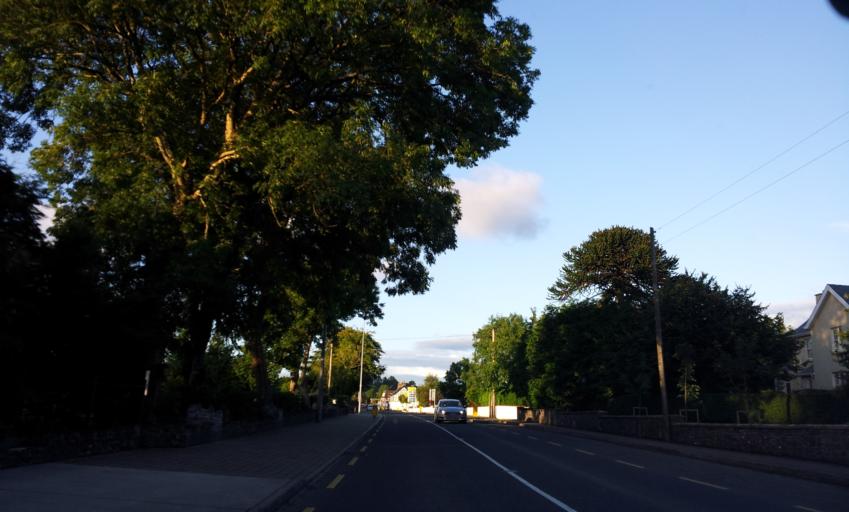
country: IE
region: Munster
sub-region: County Limerick
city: Abbeyfeale
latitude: 52.3952
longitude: -9.1783
